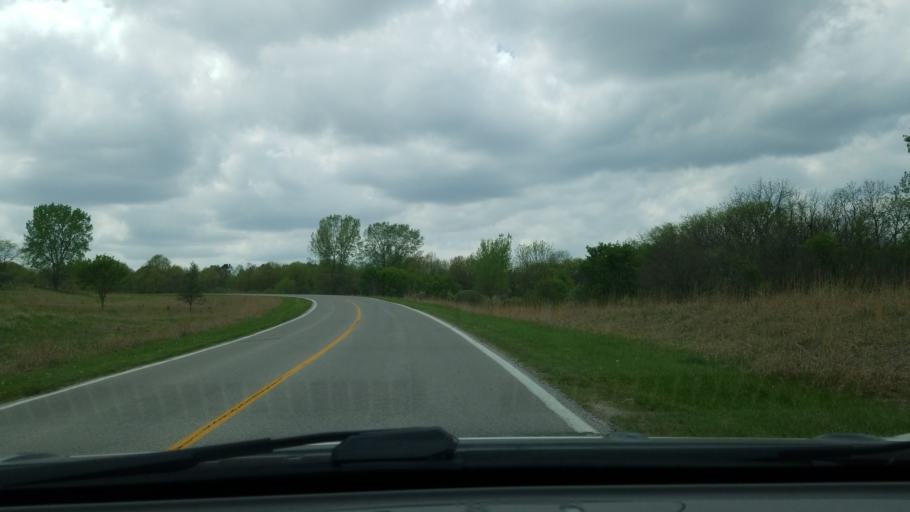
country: US
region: Nebraska
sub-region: Sarpy County
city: Chalco
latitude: 41.1704
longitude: -96.1651
